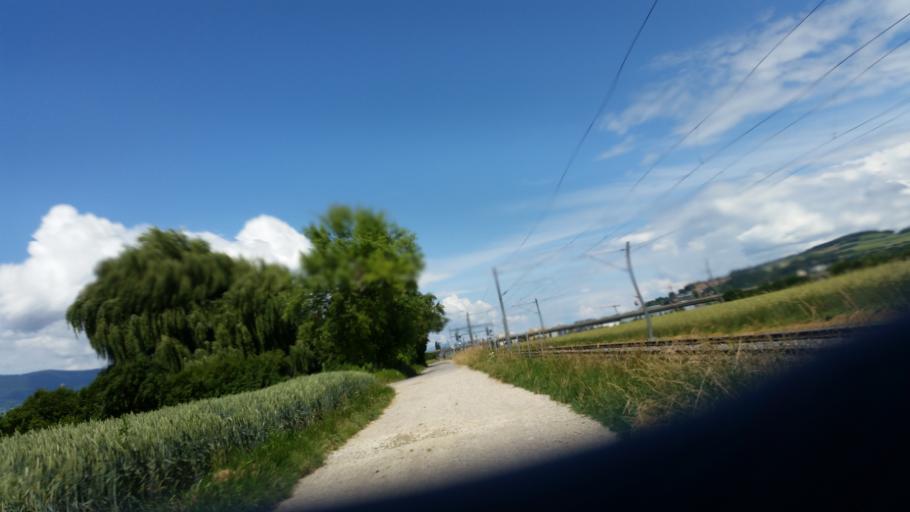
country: CH
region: Vaud
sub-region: Jura-Nord vaudois District
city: Yverdon-les-Bains
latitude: 46.7589
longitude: 6.6276
